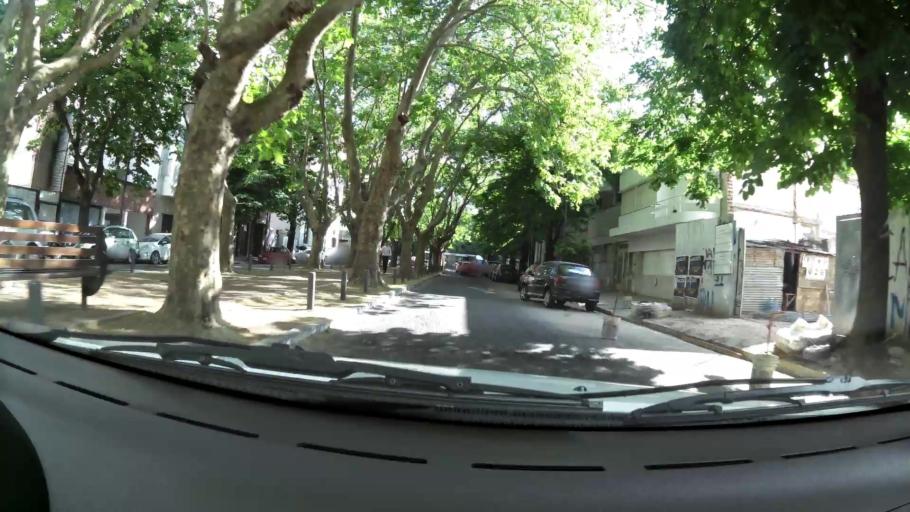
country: AR
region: Buenos Aires
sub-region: Partido de La Plata
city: La Plata
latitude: -34.9119
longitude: -57.9453
